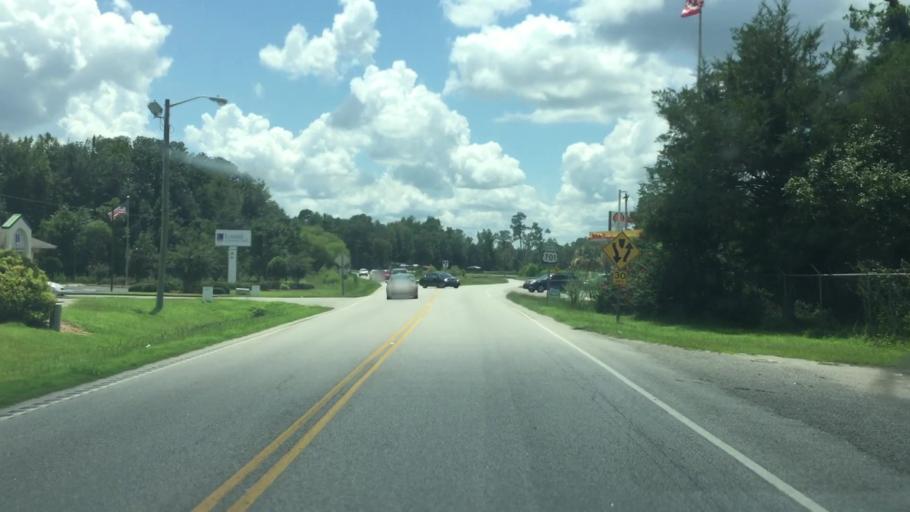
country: US
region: North Carolina
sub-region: Columbus County
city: Tabor City
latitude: 34.1343
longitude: -78.8752
